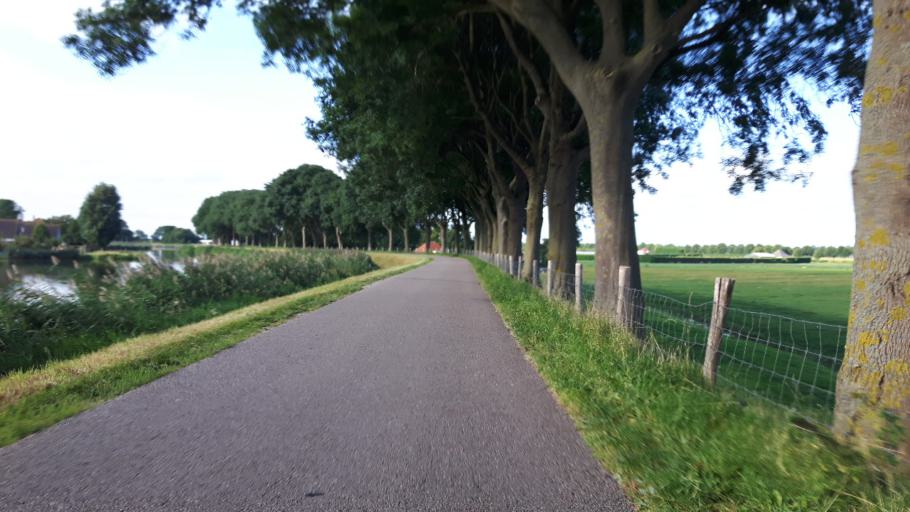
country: NL
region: North Holland
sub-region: Gemeente Purmerend
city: Purmerend
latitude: 52.5648
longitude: 4.9811
